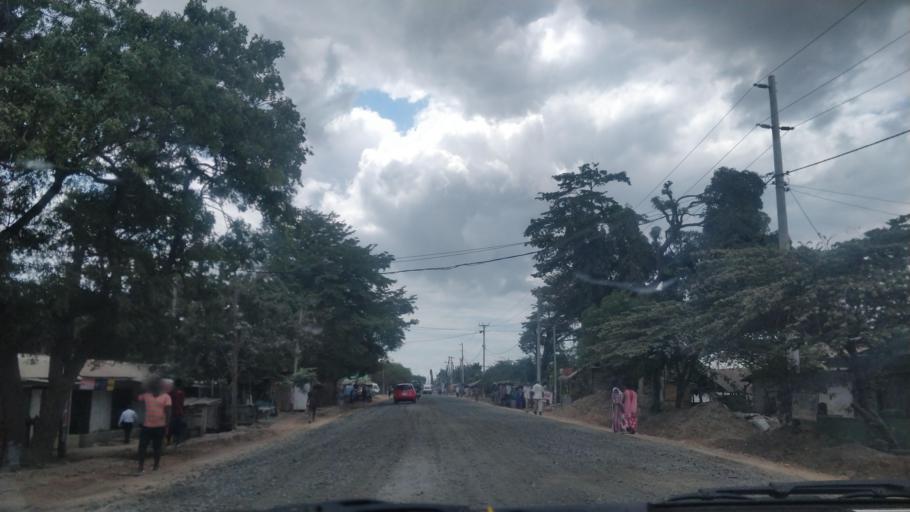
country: TZ
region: Dar es Salaam
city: Magomeni
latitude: -6.8074
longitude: 39.2227
